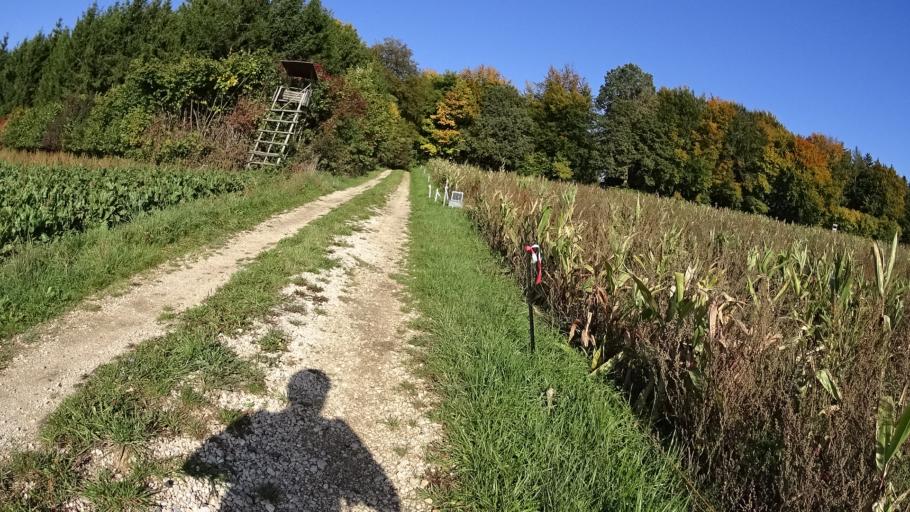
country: DE
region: Bavaria
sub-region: Upper Bavaria
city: Bohmfeld
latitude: 48.8724
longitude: 11.3552
